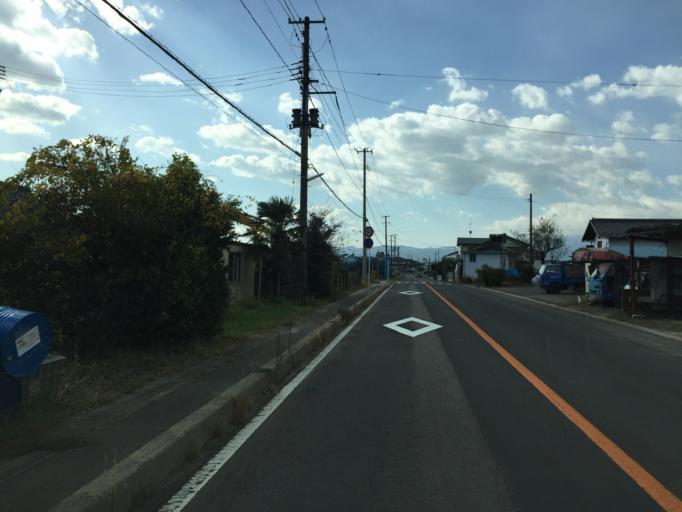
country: JP
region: Fukushima
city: Fukushima-shi
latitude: 37.7924
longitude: 140.4004
